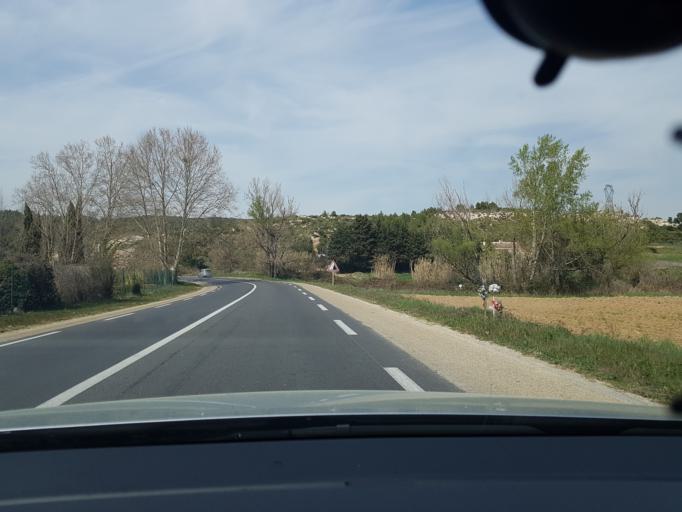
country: FR
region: Provence-Alpes-Cote d'Azur
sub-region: Departement des Bouches-du-Rhone
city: Gardanne
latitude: 43.4697
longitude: 5.4610
